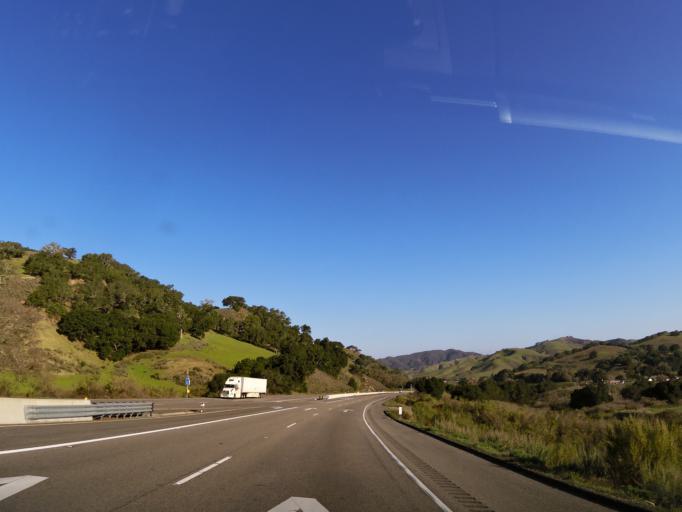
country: US
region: California
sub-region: Santa Barbara County
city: Buellton
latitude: 34.5393
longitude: -120.1970
